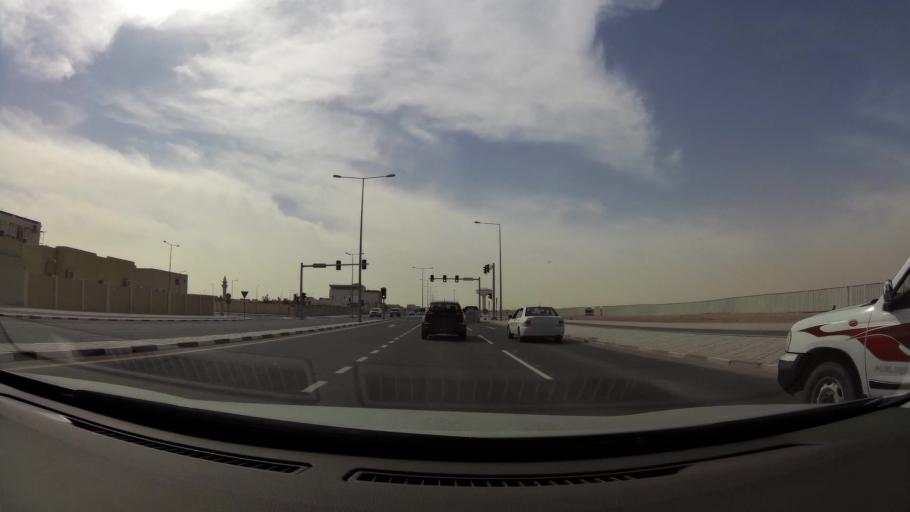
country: QA
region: Baladiyat ar Rayyan
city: Ar Rayyan
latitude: 25.3181
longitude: 51.4100
